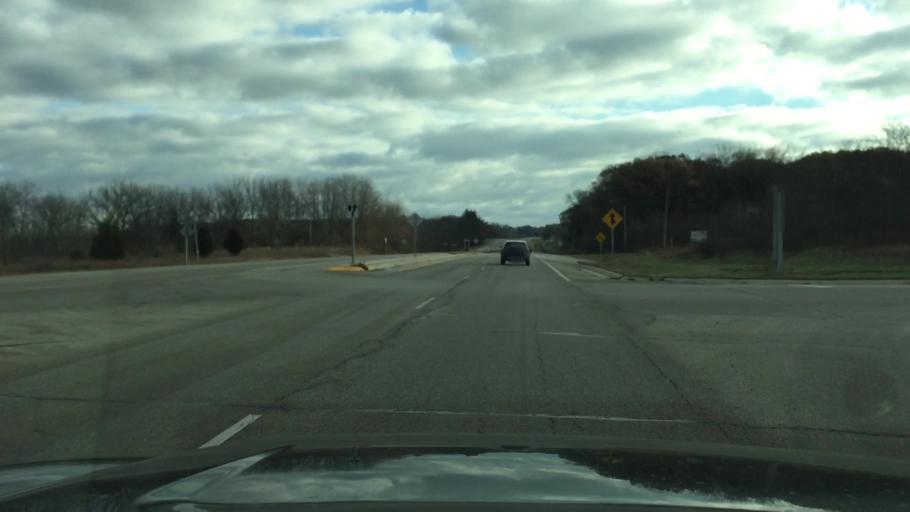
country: US
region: Wisconsin
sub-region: Walworth County
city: Williams Bay
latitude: 42.5828
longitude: -88.5195
